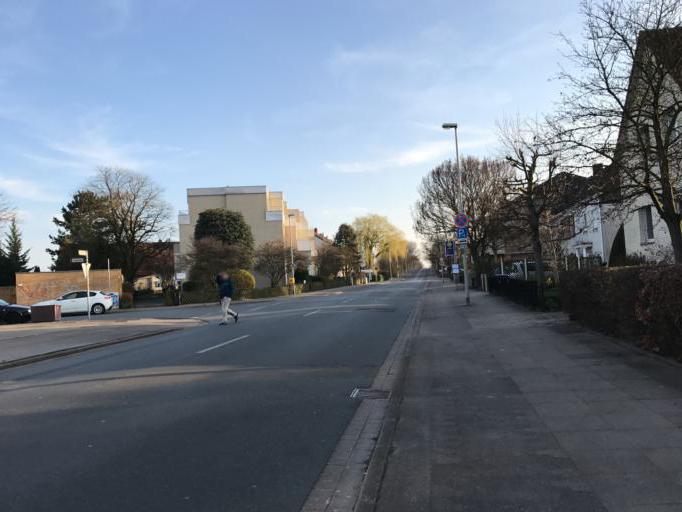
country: DE
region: Lower Saxony
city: Laatzen
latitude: 52.3477
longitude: 9.7814
